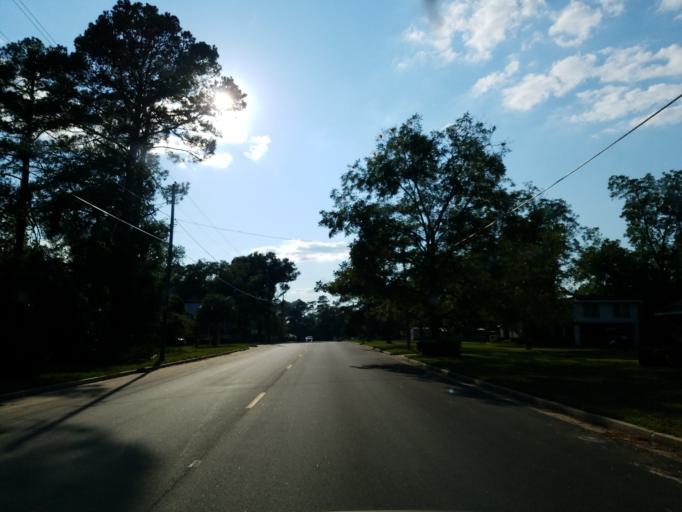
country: US
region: Georgia
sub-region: Cook County
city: Sparks
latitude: 31.1672
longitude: -83.4415
